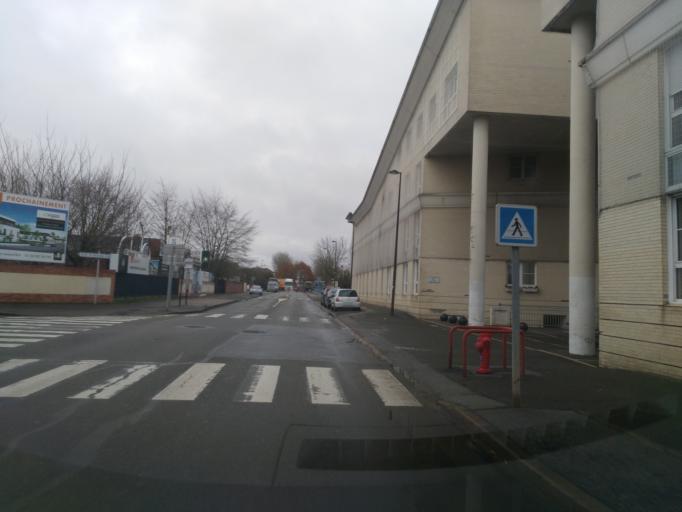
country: FR
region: Ile-de-France
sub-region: Departement des Yvelines
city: Voisins-le-Bretonneux
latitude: 48.7667
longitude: 2.0561
